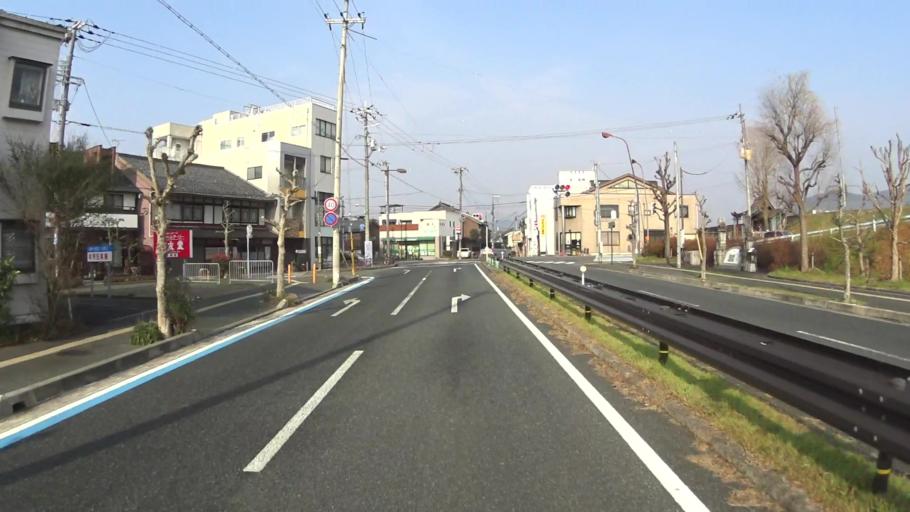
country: JP
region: Kyoto
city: Fukuchiyama
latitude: 35.3018
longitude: 135.1269
